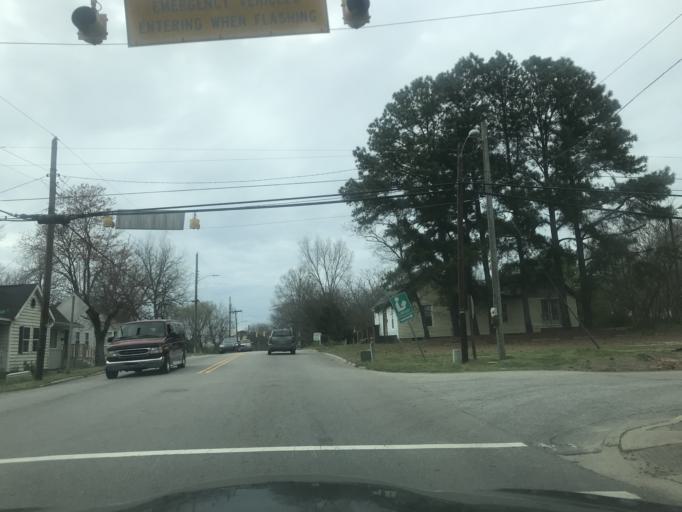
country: US
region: North Carolina
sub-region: Franklin County
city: Franklinton
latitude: 36.1026
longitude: -78.4594
